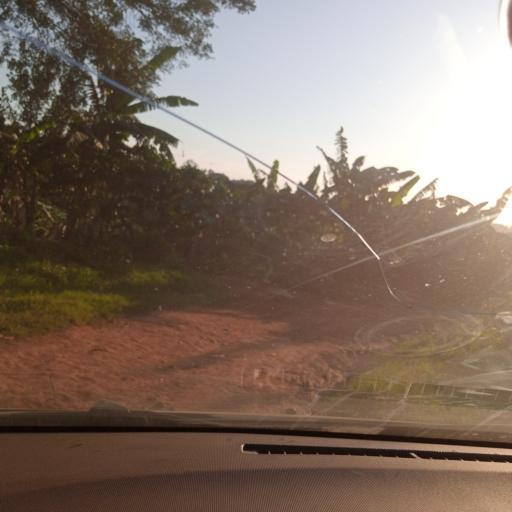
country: UG
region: Central Region
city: Masaka
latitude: -0.3375
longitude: 31.7592
